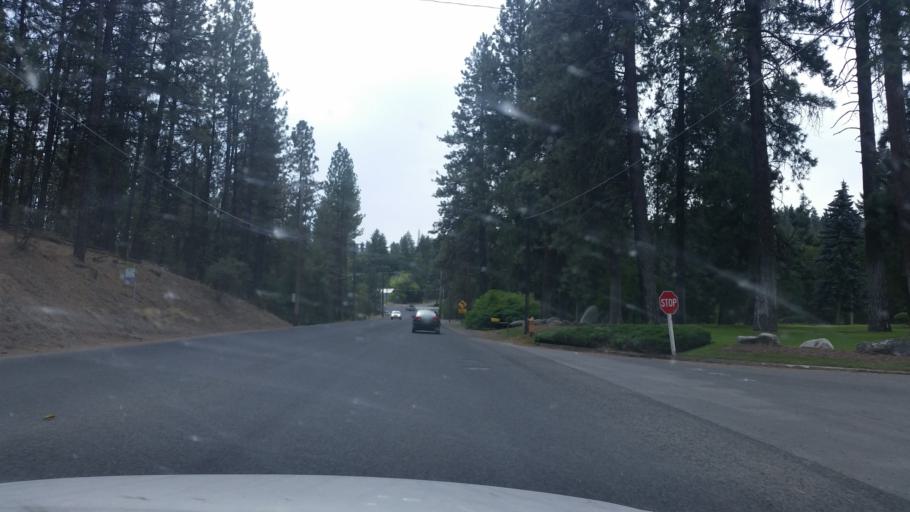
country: US
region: Washington
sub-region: Spokane County
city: Spokane
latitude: 47.6587
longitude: -117.4655
